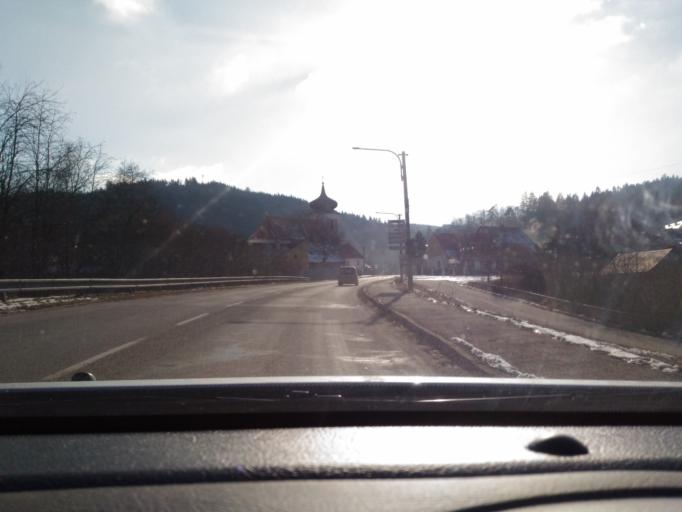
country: CZ
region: South Moravian
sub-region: Okres Brno-Venkov
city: Nedvedice
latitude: 49.4583
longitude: 16.3349
